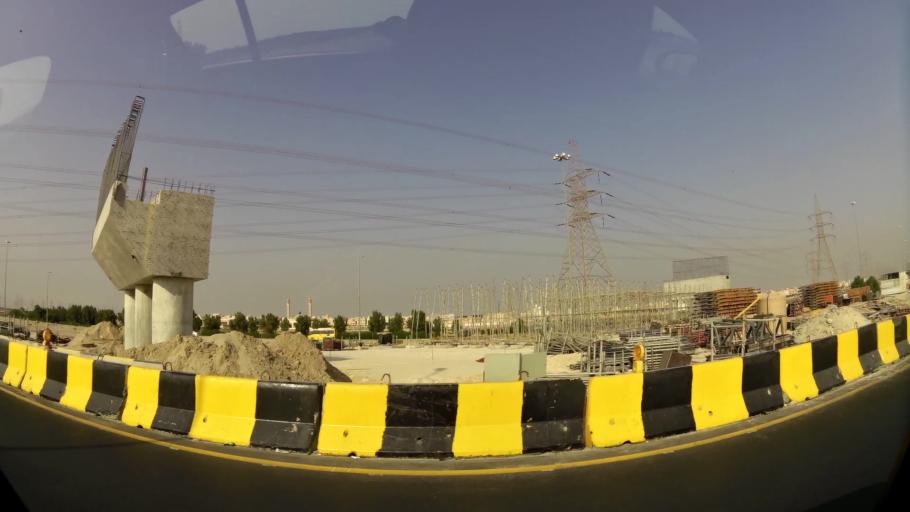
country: KW
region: Muhafazat al Jahra'
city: Al Jahra'
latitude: 29.2958
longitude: 47.7886
